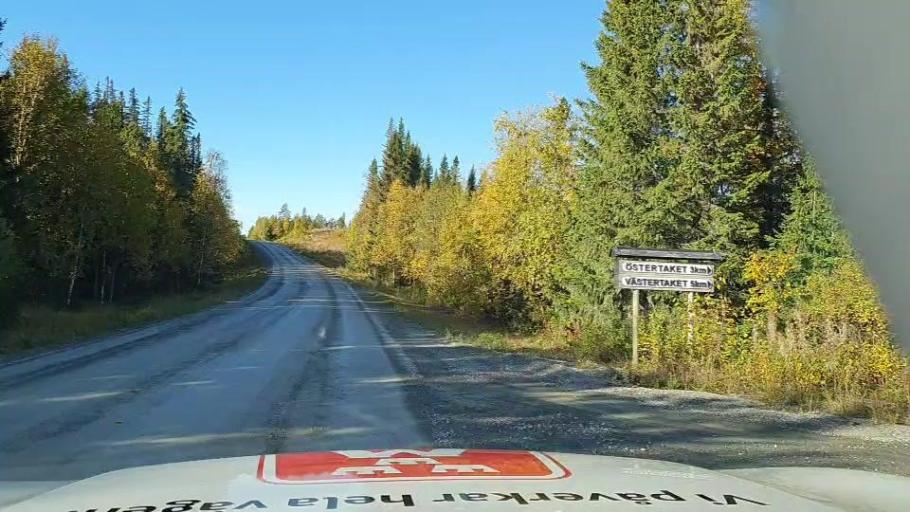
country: SE
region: Jaemtland
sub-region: Bergs Kommun
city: Hoverberg
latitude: 62.9082
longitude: 14.2698
